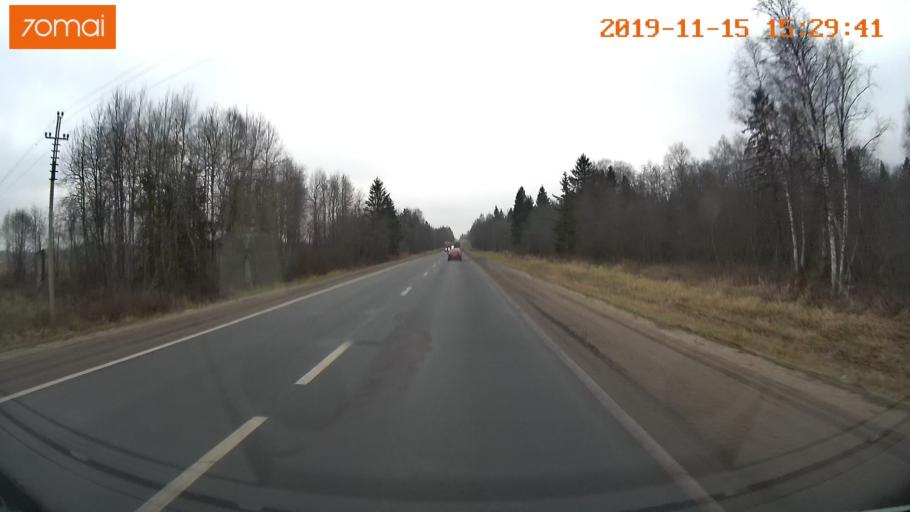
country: RU
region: Jaroslavl
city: Danilov
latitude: 58.1180
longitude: 40.1178
